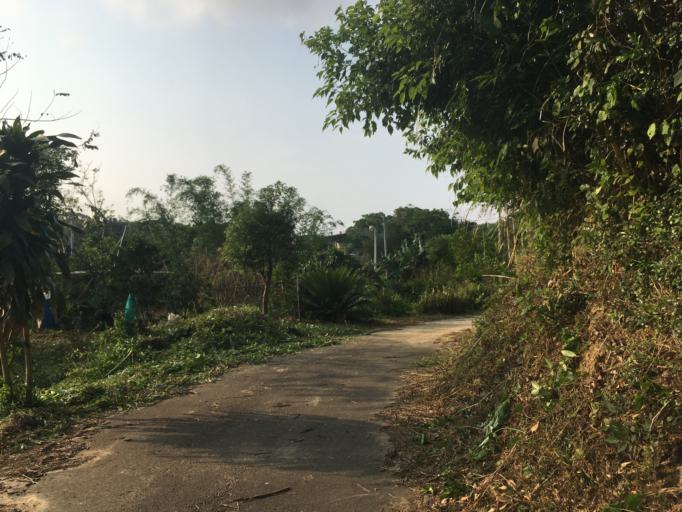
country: TW
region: Taiwan
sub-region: Hsinchu
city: Hsinchu
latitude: 24.7632
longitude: 120.9670
